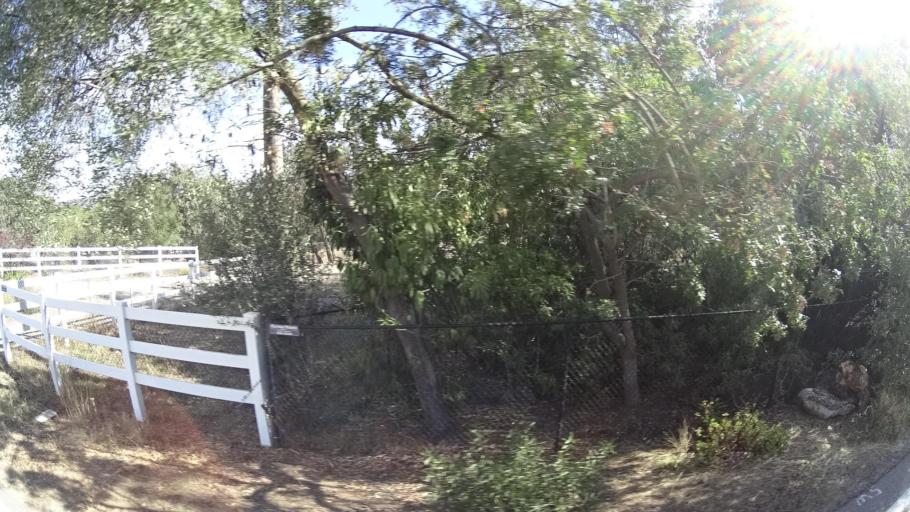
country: US
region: California
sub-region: San Diego County
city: Alpine
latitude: 32.8221
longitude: -116.7868
